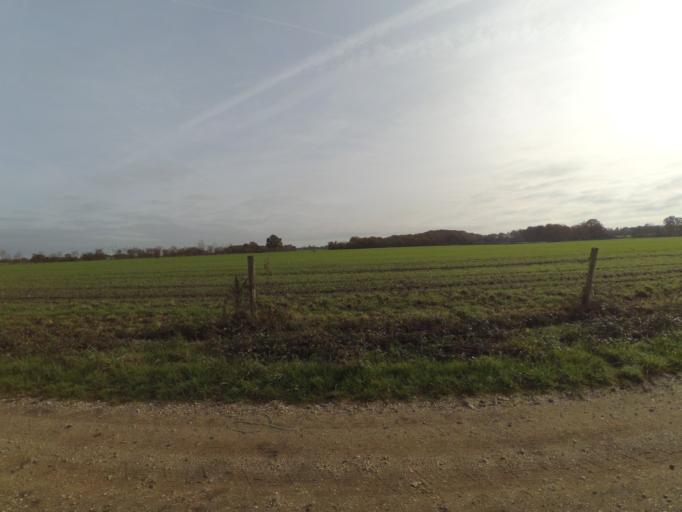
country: FR
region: Pays de la Loire
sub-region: Departement de la Loire-Atlantique
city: La Planche
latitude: 47.0056
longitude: -1.4019
